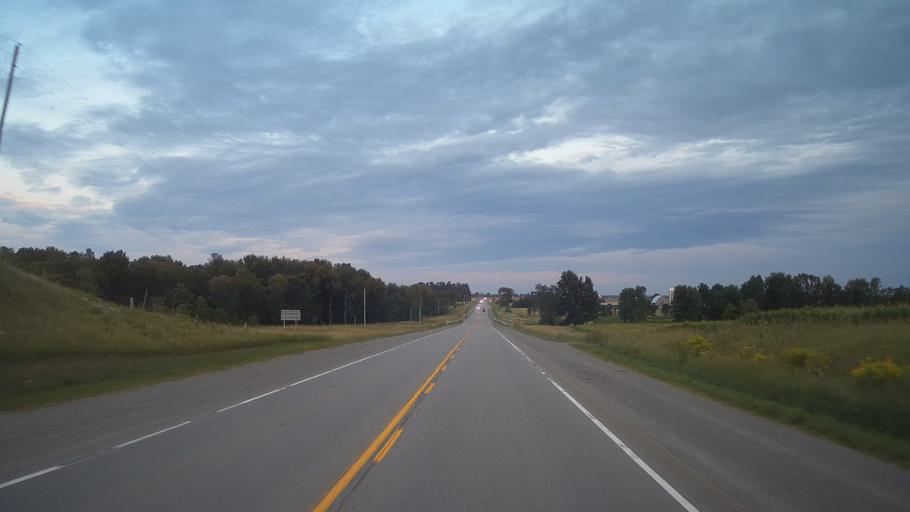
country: CA
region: Ontario
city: Pembroke
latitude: 45.6948
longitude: -76.9586
